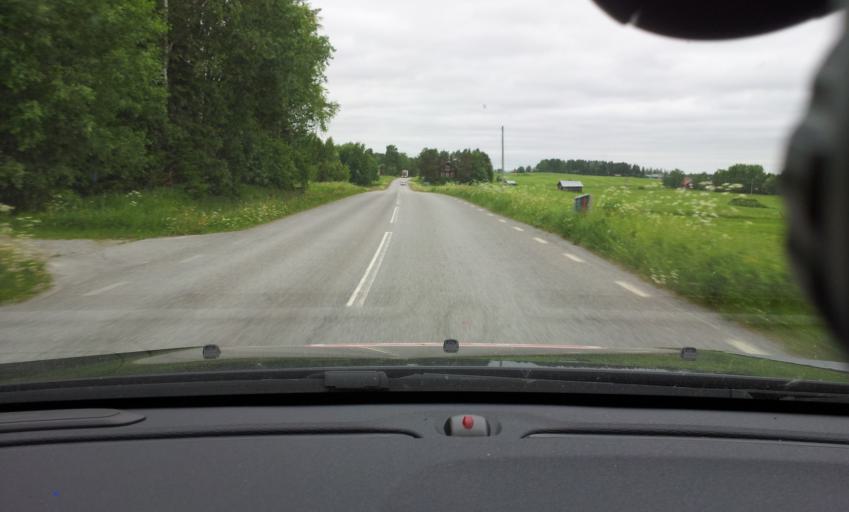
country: SE
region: Jaemtland
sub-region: Krokoms Kommun
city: Krokom
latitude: 63.1373
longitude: 14.1943
